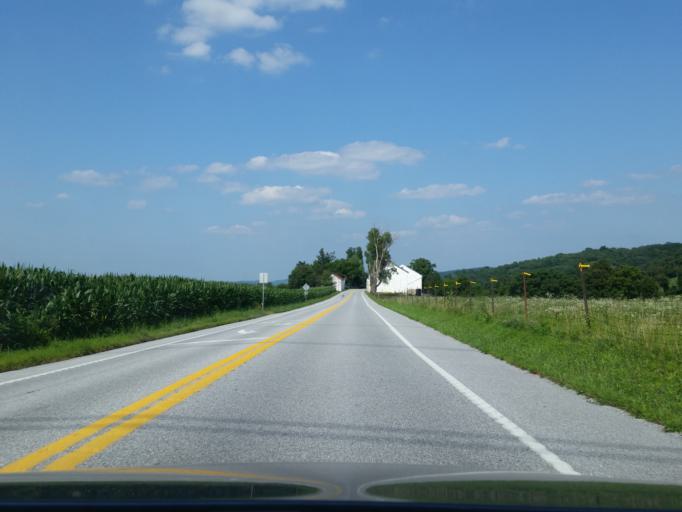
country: US
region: Pennsylvania
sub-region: York County
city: Hallam
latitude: 39.9831
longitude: -76.6139
